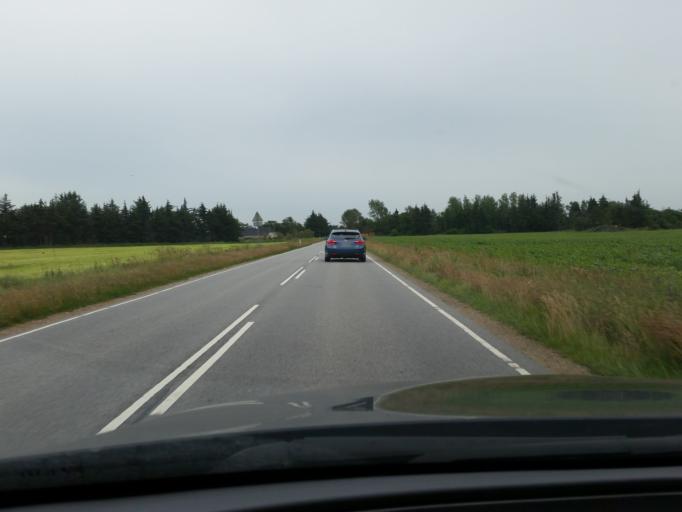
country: DK
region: South Denmark
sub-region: Varde Kommune
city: Oksbol
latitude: 55.8009
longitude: 8.2297
